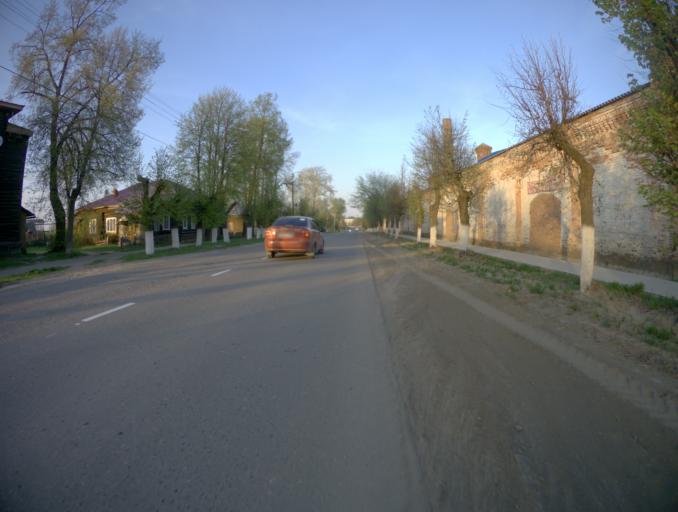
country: RU
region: Ivanovo
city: Yuzha
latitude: 56.5841
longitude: 42.0182
